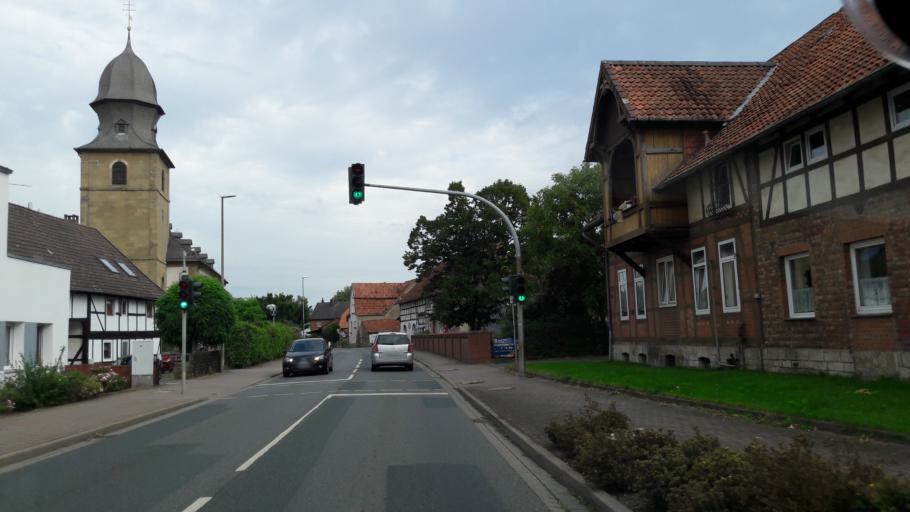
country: DE
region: Lower Saxony
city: Bad Salzdetfurth
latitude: 52.0947
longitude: 10.0184
